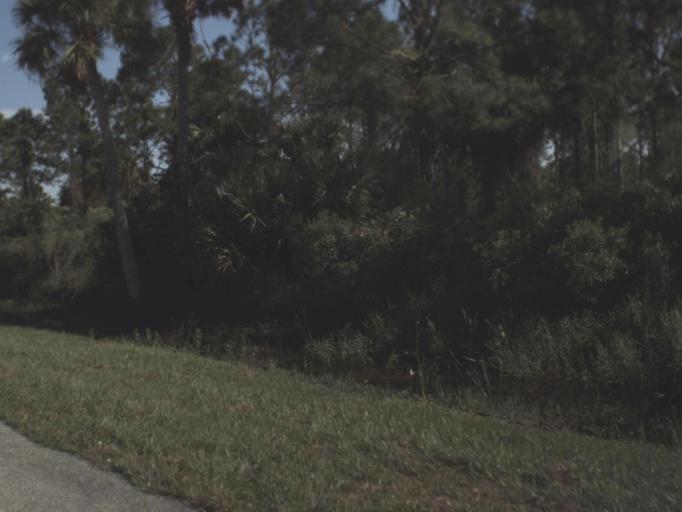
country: US
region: Florida
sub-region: Glades County
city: Moore Haven
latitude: 26.9007
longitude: -81.2424
